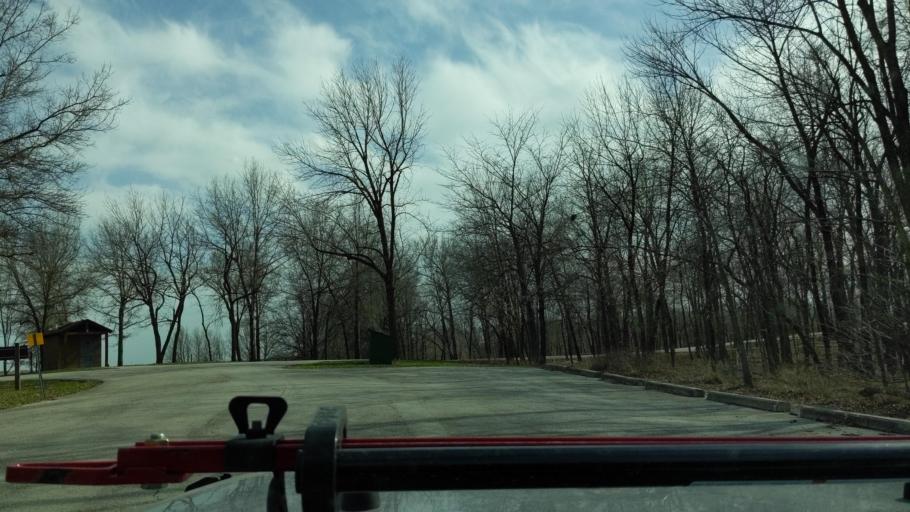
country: US
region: Missouri
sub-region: Macon County
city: Macon
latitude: 39.7701
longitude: -92.5182
